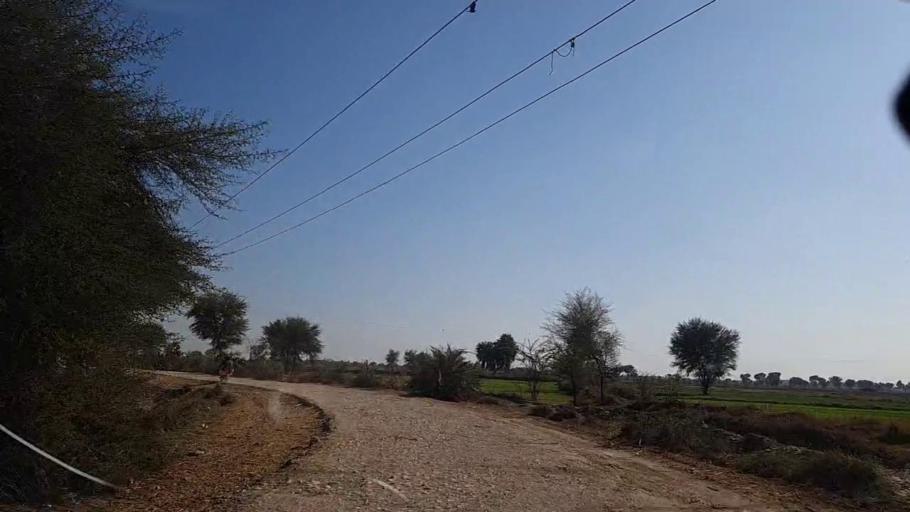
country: PK
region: Sindh
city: Khanpur
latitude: 27.8045
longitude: 69.3700
